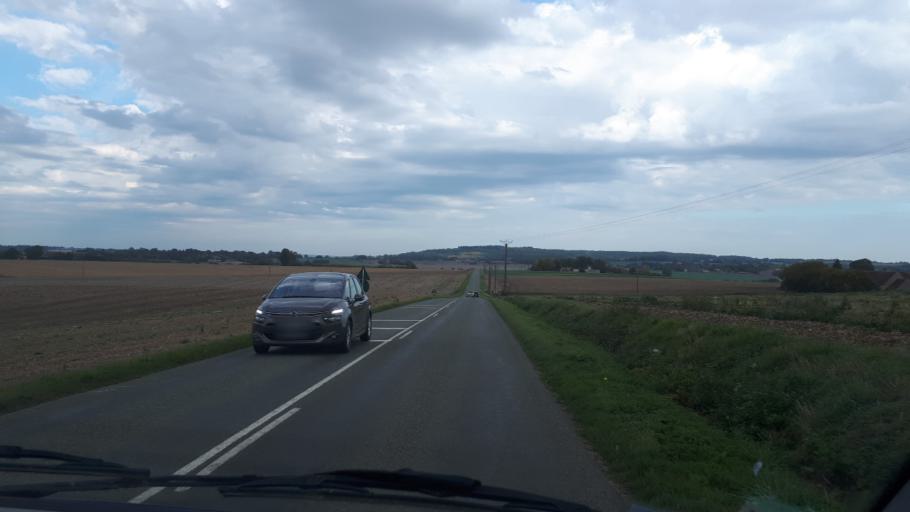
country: FR
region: Centre
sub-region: Departement d'Eure-et-Loir
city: Authon-du-Perche
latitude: 48.2156
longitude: 0.8797
